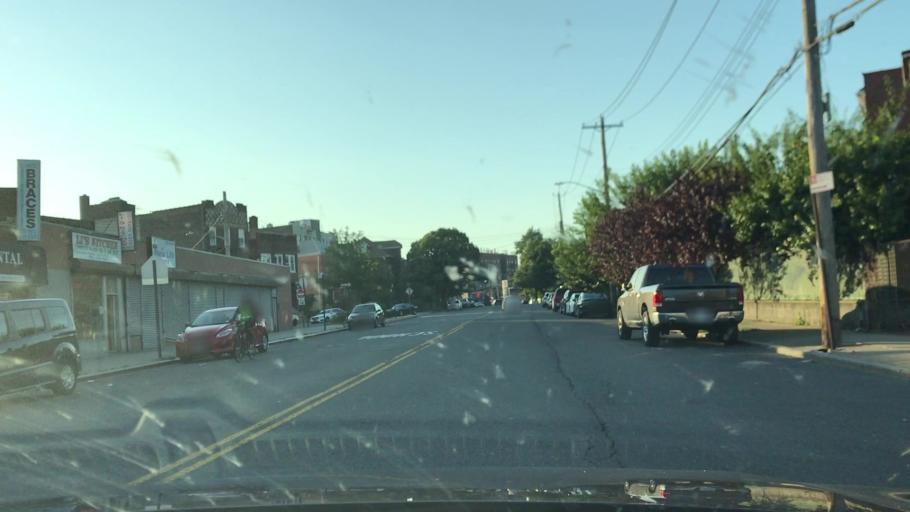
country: US
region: New York
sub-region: Bronx
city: The Bronx
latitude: 40.8632
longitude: -73.8582
